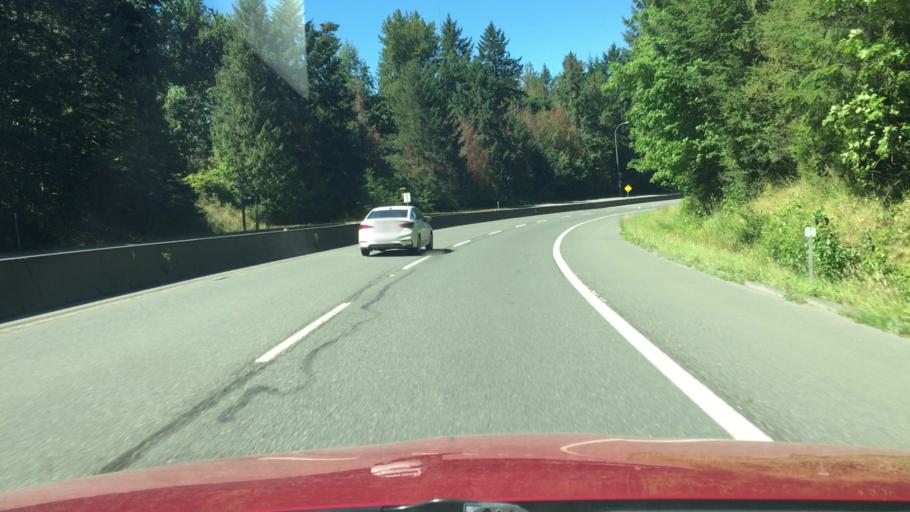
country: CA
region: British Columbia
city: North Saanich
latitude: 48.6733
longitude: -123.4289
